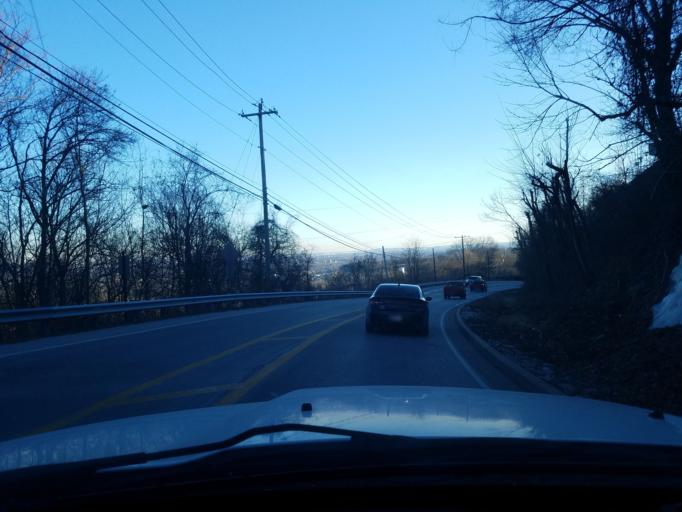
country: US
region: Indiana
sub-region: Floyd County
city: New Albany
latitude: 38.3239
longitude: -85.8576
